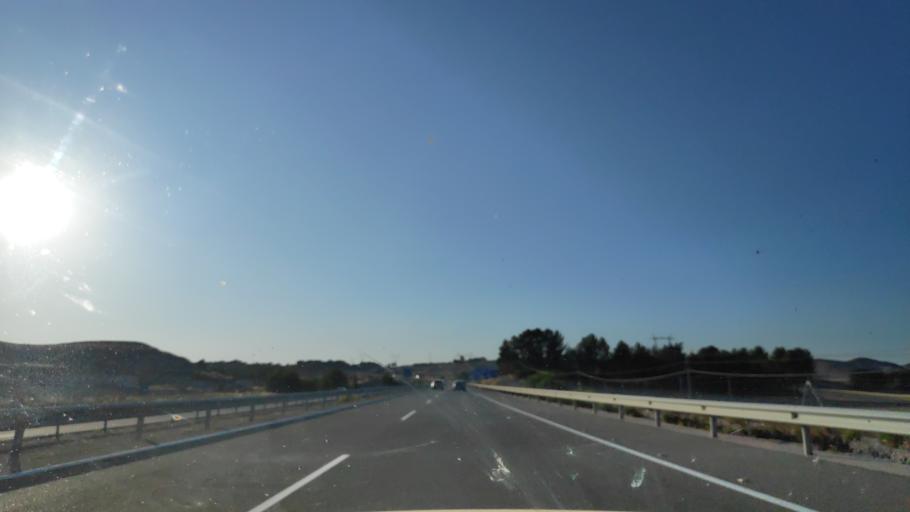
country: ES
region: Castille-La Mancha
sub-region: Provincia de Cuenca
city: Belinchon
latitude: 40.0369
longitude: -3.0473
